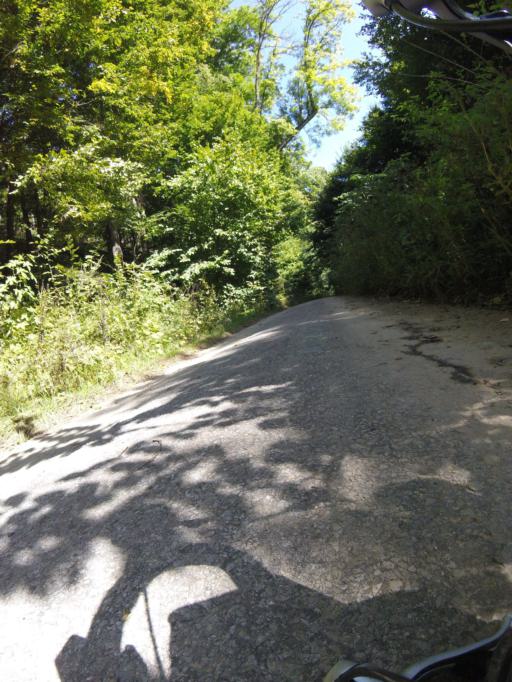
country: HU
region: Borsod-Abauj-Zemplen
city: Saly
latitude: 48.0823
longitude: 20.5894
